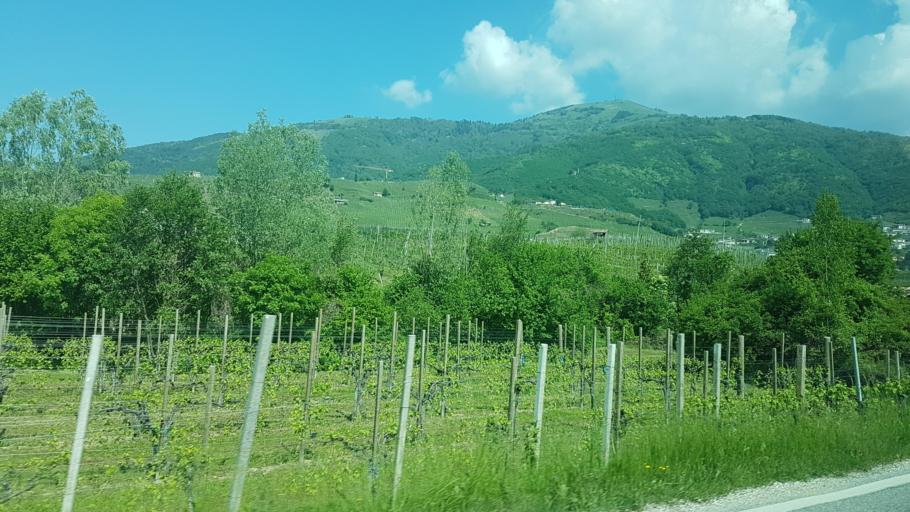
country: IT
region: Veneto
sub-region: Provincia di Treviso
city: Vidor
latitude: 45.8925
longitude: 12.0374
